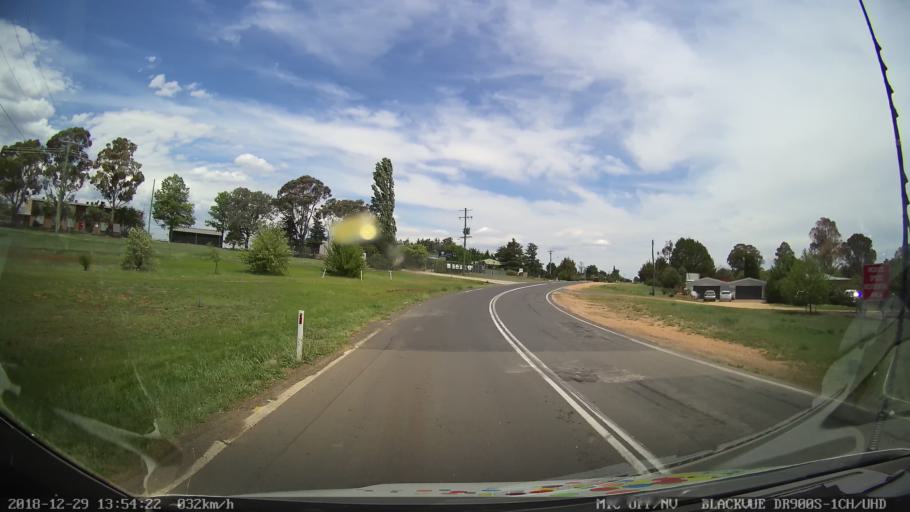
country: AU
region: New South Wales
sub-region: Cooma-Monaro
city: Cooma
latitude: -36.2137
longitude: 149.1522
